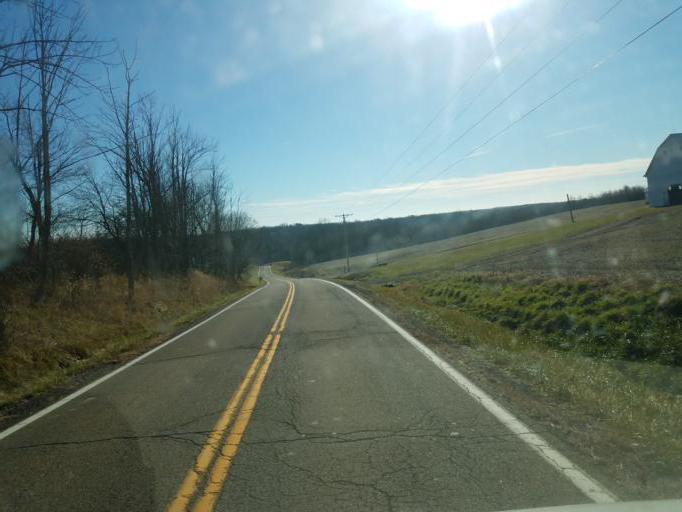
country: US
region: Ohio
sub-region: Muskingum County
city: Frazeysburg
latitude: 40.2788
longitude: -82.1331
